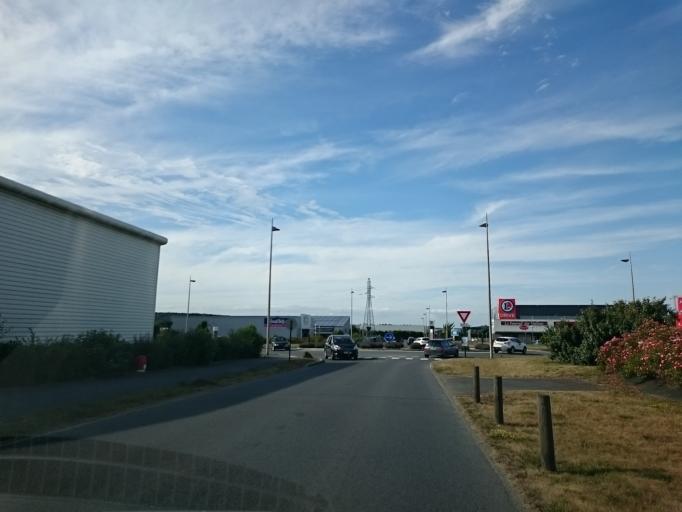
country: FR
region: Brittany
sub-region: Departement d'Ille-et-Vilaine
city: Bain-de-Bretagne
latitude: 47.8549
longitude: -1.6892
